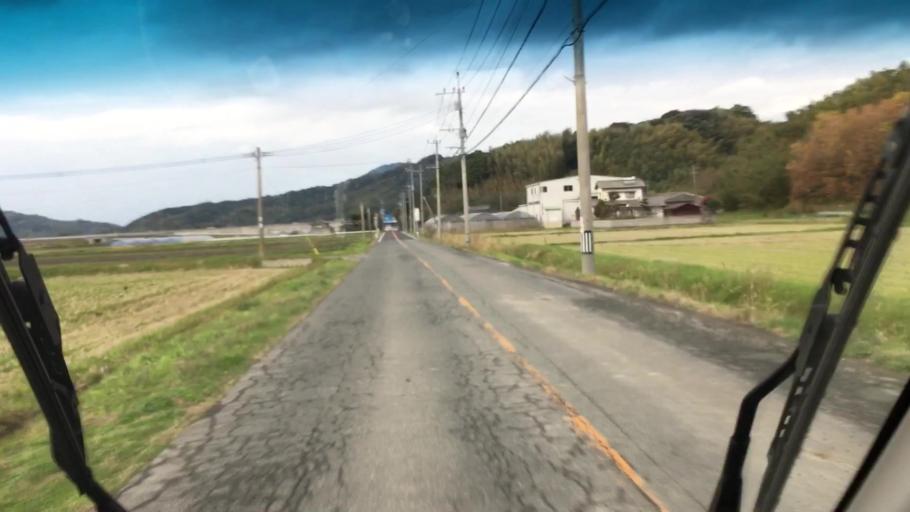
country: JP
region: Fukuoka
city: Maebaru-chuo
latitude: 33.5271
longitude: 130.1906
